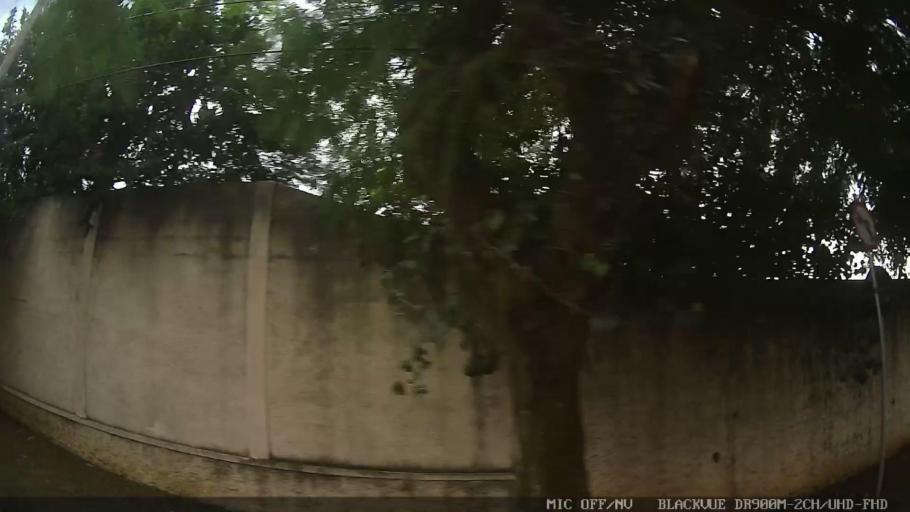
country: BR
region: Sao Paulo
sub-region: Atibaia
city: Atibaia
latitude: -23.1300
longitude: -46.5563
